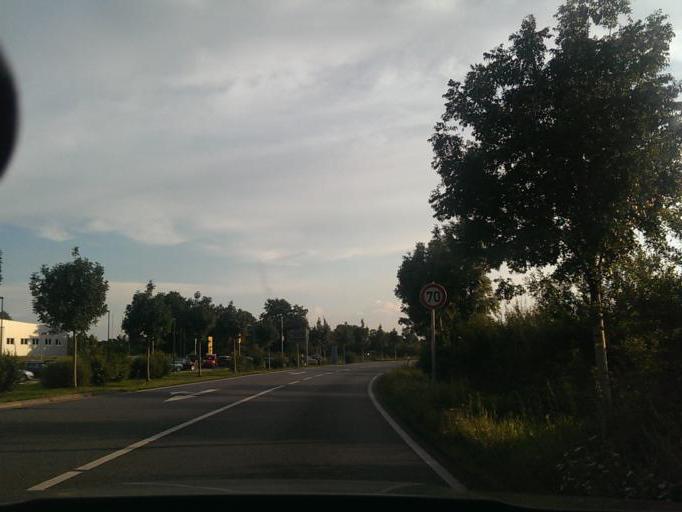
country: DE
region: Lower Saxony
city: Lilienthal
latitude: 53.1606
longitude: 8.9130
